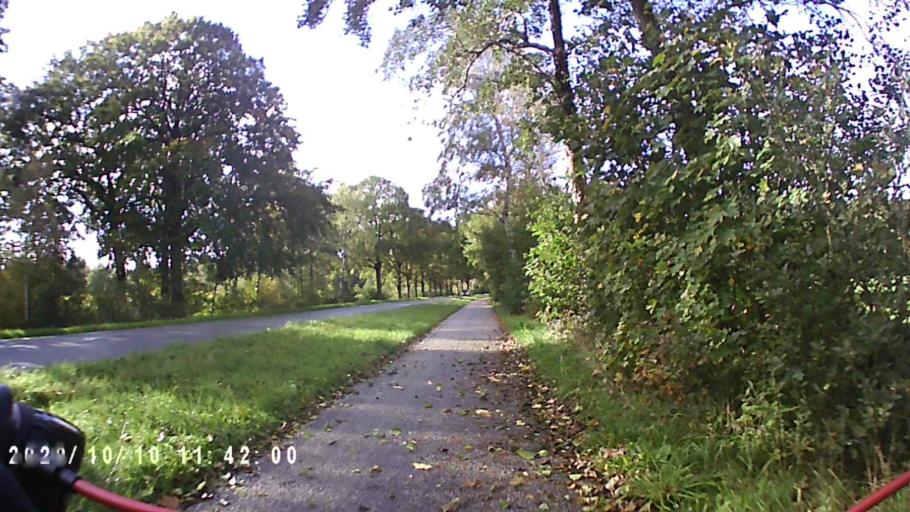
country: NL
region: Friesland
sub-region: Gemeente Smallingerland
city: Drachten
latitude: 53.0633
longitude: 6.0994
